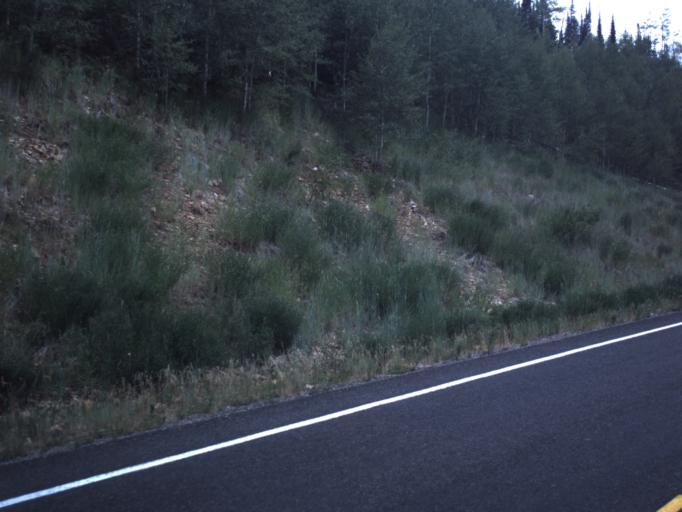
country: US
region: Utah
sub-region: Summit County
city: Francis
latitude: 40.5158
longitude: -111.0681
